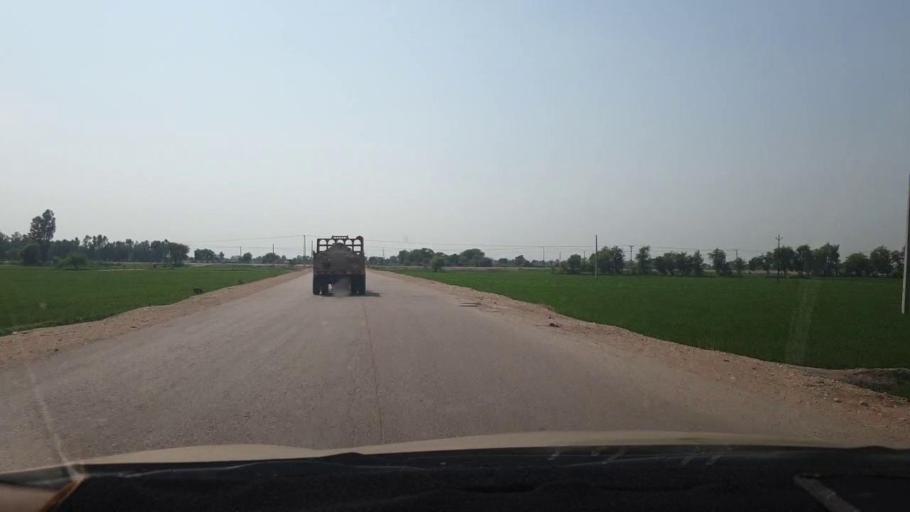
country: PK
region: Sindh
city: Larkana
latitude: 27.6110
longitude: 68.2359
